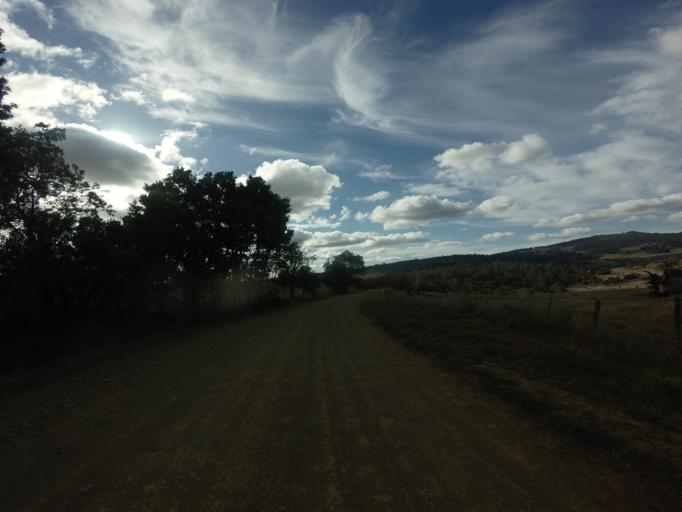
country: AU
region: Tasmania
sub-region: Brighton
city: Bridgewater
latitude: -42.4523
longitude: 147.2419
